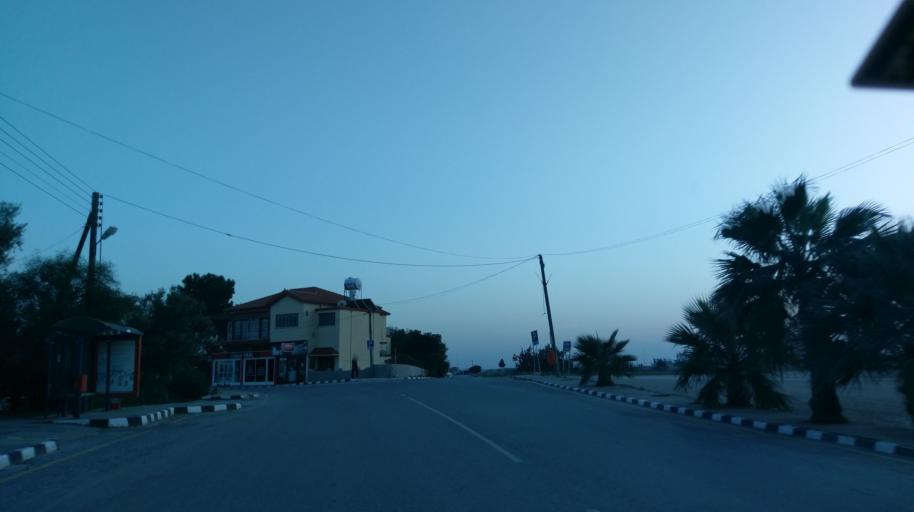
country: CY
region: Ammochostos
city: Trikomo
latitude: 35.2824
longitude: 33.8933
